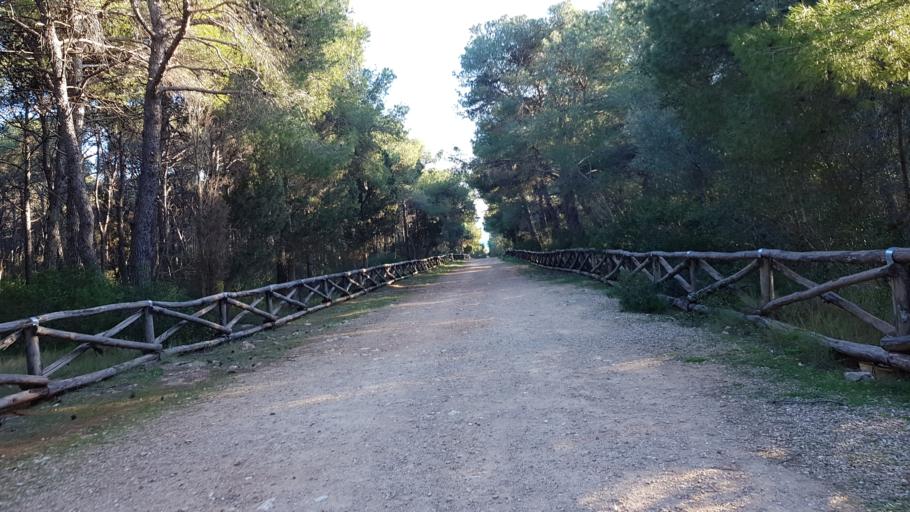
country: IT
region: Apulia
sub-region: Provincia di Lecce
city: Nardo
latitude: 40.1515
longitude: 17.9713
